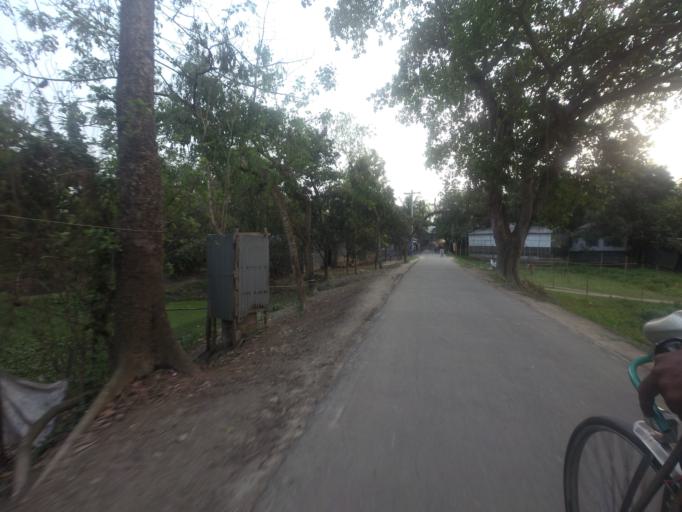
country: BD
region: Rajshahi
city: Sirajganj
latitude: 24.3319
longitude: 89.6817
